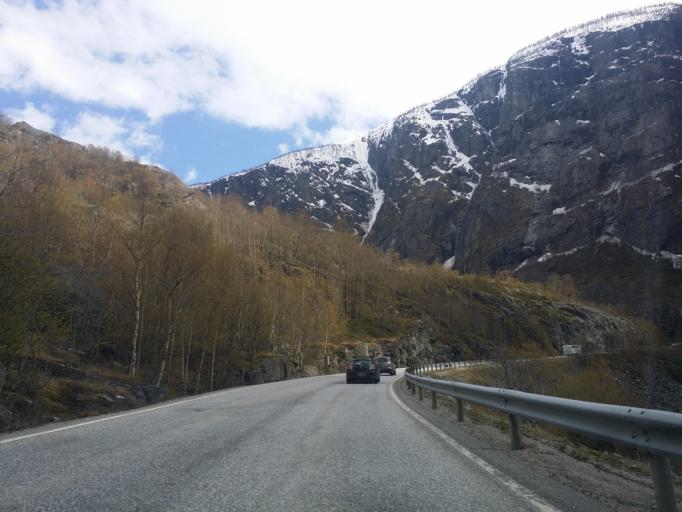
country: NO
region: Hordaland
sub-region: Eidfjord
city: Eidfjord
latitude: 60.4198
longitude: 7.1905
